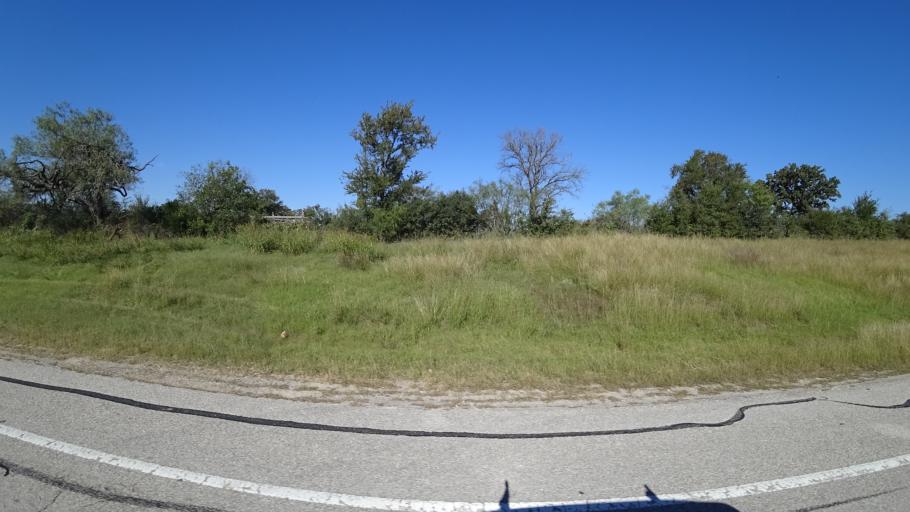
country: US
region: Texas
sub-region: Travis County
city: Hornsby Bend
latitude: 30.2596
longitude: -97.6103
